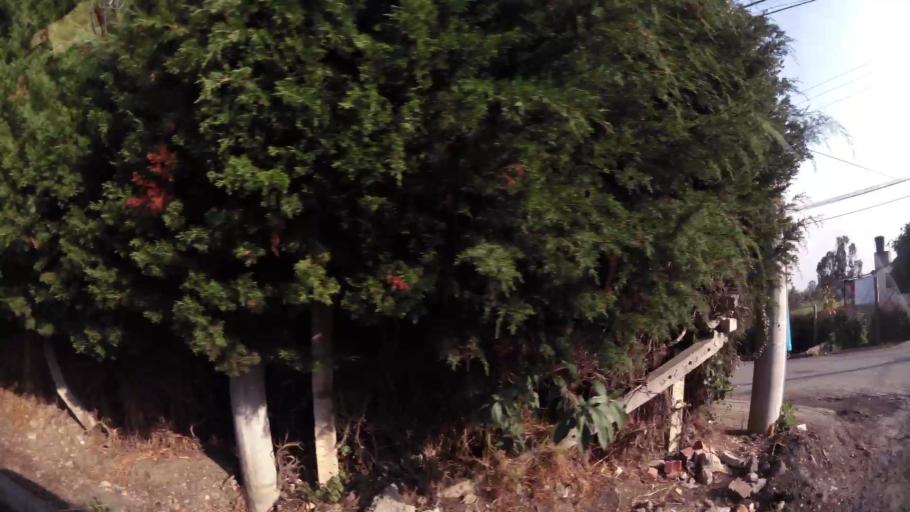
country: CO
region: Cundinamarca
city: Cota
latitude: 4.8062
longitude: -74.1127
